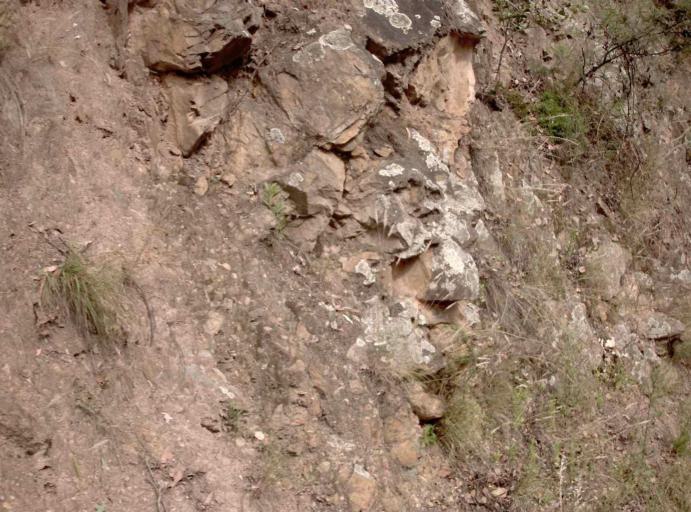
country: AU
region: Victoria
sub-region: Wellington
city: Heyfield
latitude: -37.7383
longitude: 146.6704
